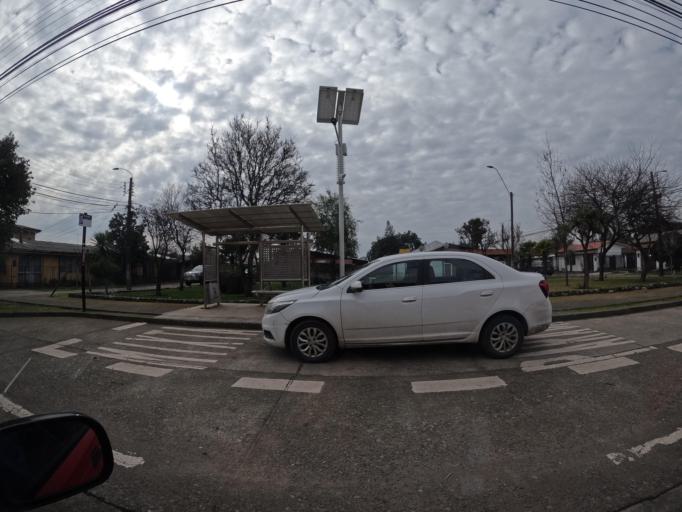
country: CL
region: Maule
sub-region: Provincia de Linares
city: Linares
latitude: -35.8367
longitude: -71.5939
